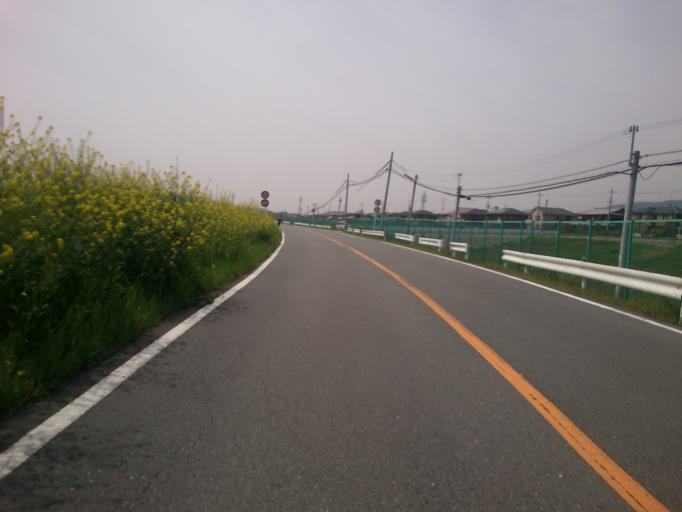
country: JP
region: Kyoto
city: Yawata
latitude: 34.9135
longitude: 135.7166
